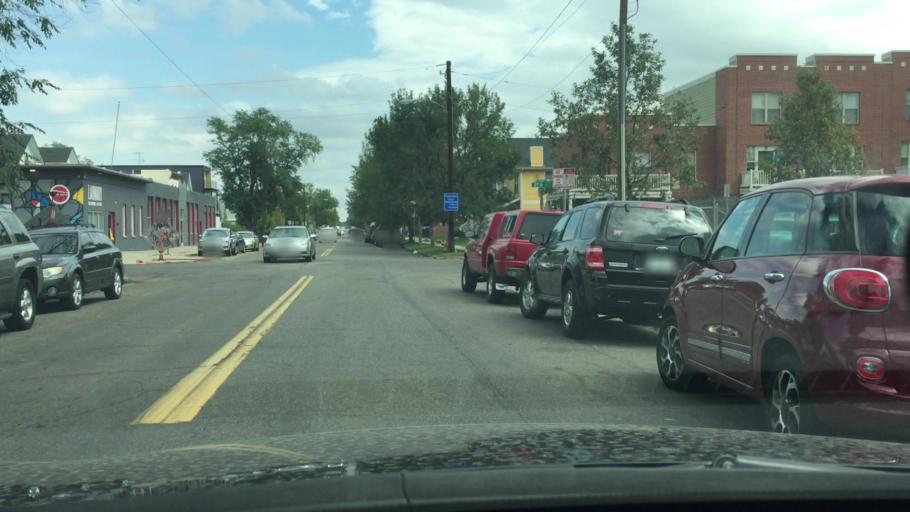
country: US
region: Colorado
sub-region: Denver County
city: Denver
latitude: 39.7586
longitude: -104.9835
